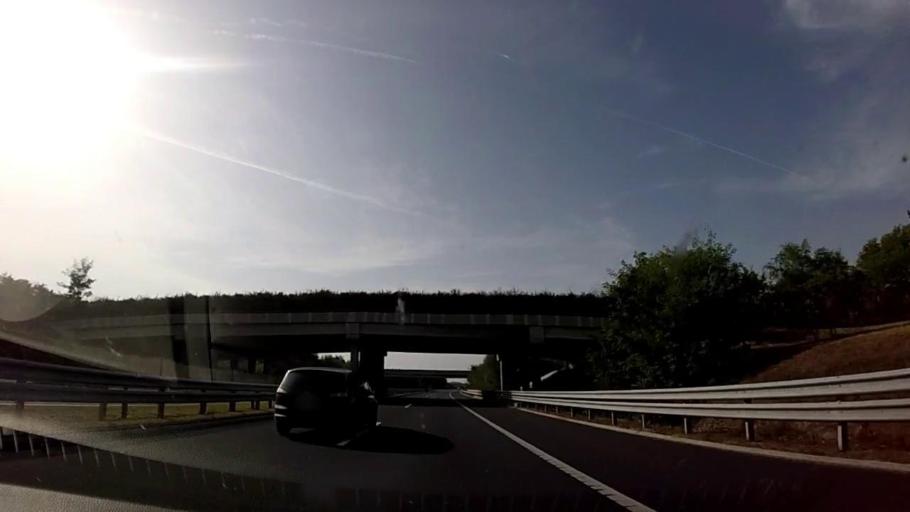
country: HU
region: Zala
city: Zalakomar
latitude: 46.5717
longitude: 17.2459
